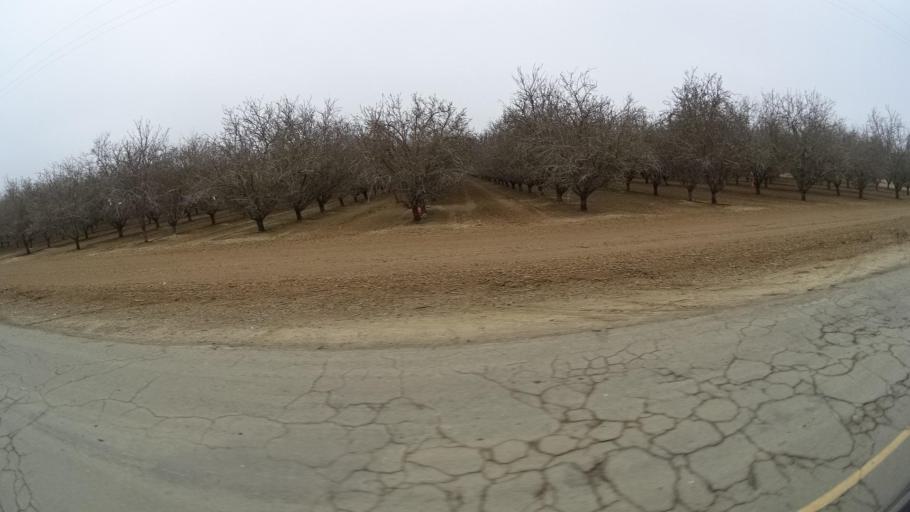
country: US
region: California
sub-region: Kern County
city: Wasco
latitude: 35.5721
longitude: -119.5025
